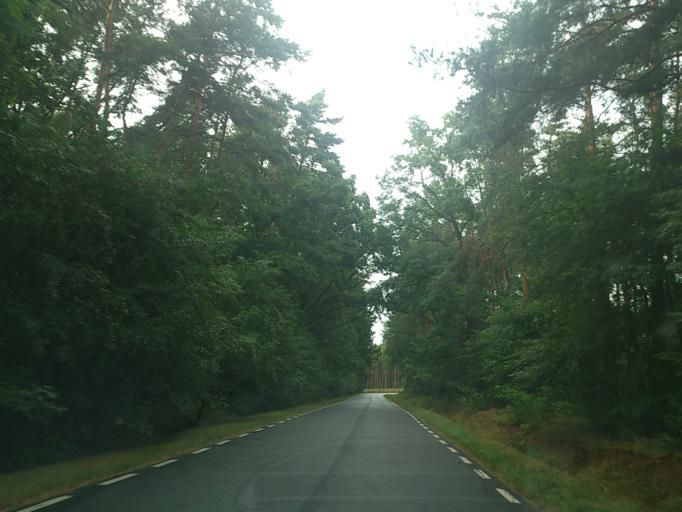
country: PL
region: Greater Poland Voivodeship
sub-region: Powiat poznanski
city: Pobiedziska
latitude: 52.5097
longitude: 17.2031
